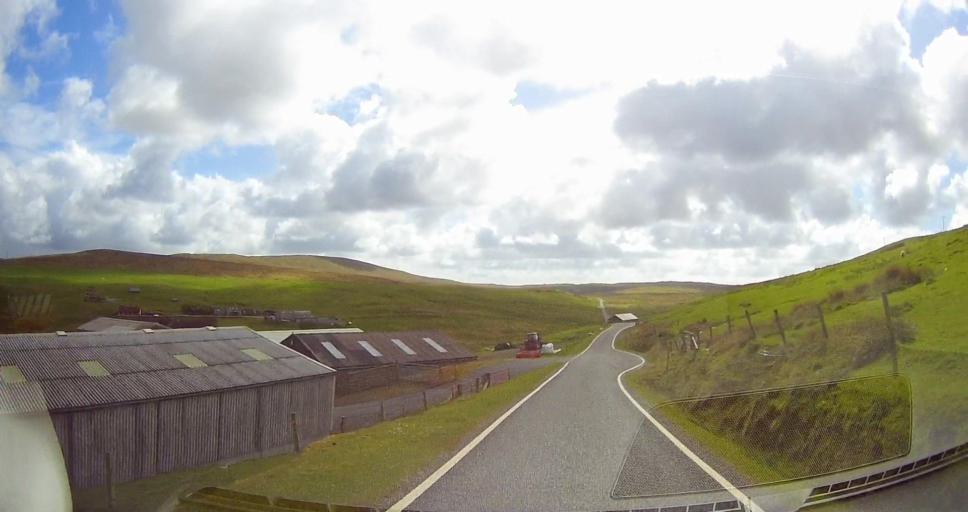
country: GB
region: Scotland
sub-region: Shetland Islands
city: Lerwick
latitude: 60.5283
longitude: -1.3675
